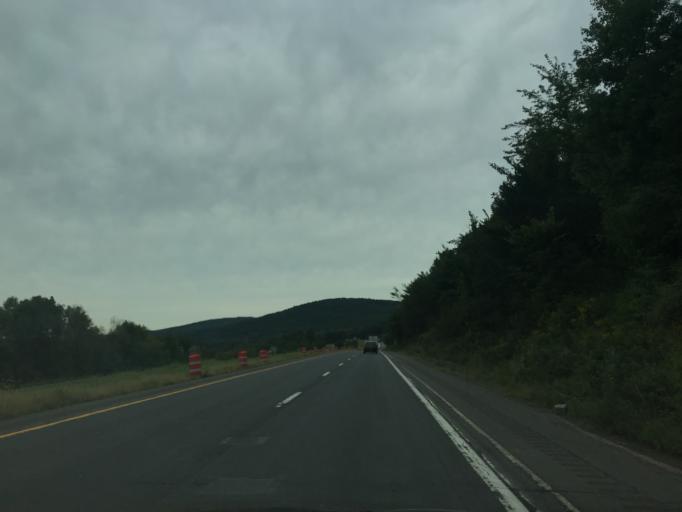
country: US
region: Pennsylvania
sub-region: Susquehanna County
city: Hallstead
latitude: 41.9943
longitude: -75.7507
